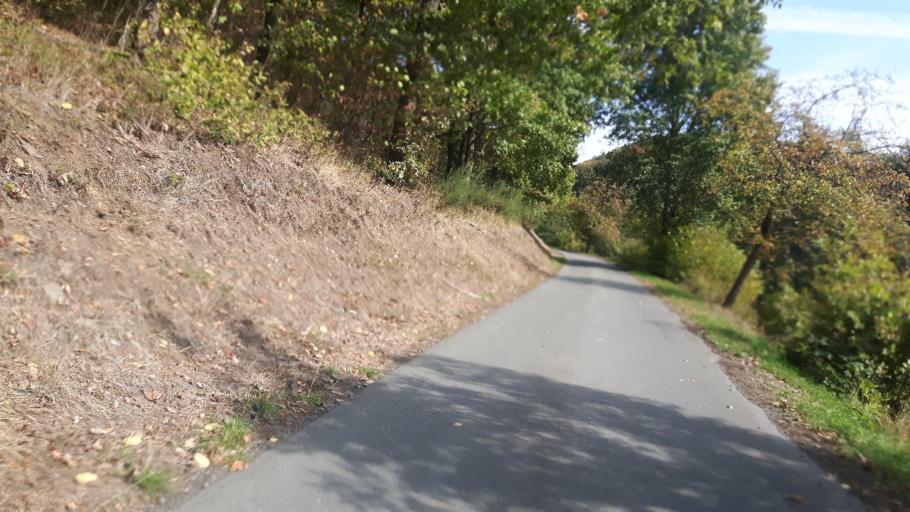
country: DE
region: North Rhine-Westphalia
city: Netphen
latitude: 50.9005
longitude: 8.2021
